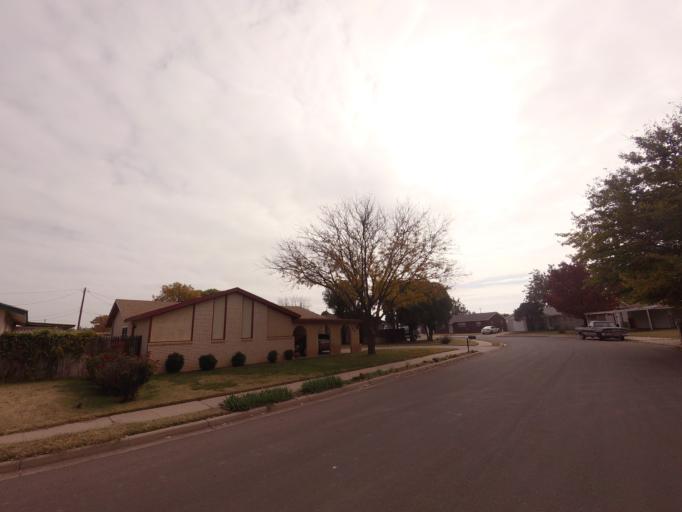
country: US
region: New Mexico
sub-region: Curry County
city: Clovis
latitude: 34.4289
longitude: -103.2189
